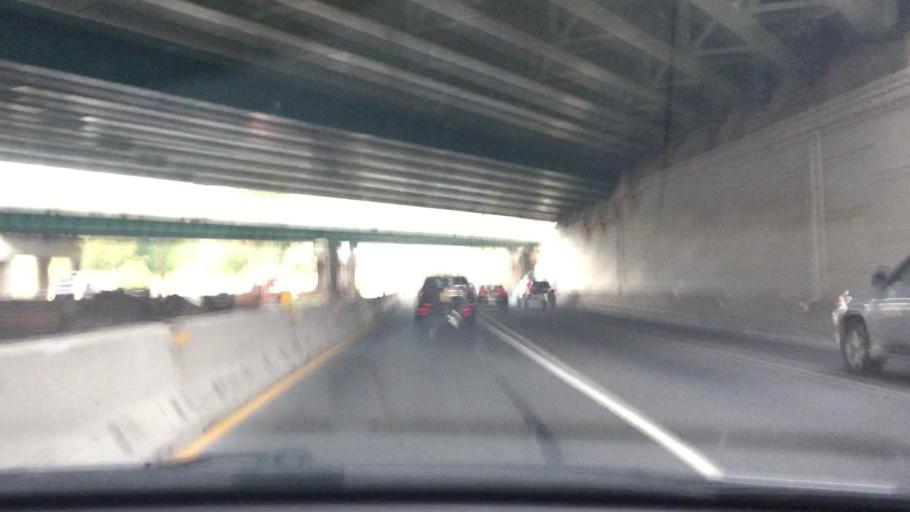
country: US
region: New Jersey
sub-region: Bergen County
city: Paramus
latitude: 40.9390
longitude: -74.0712
